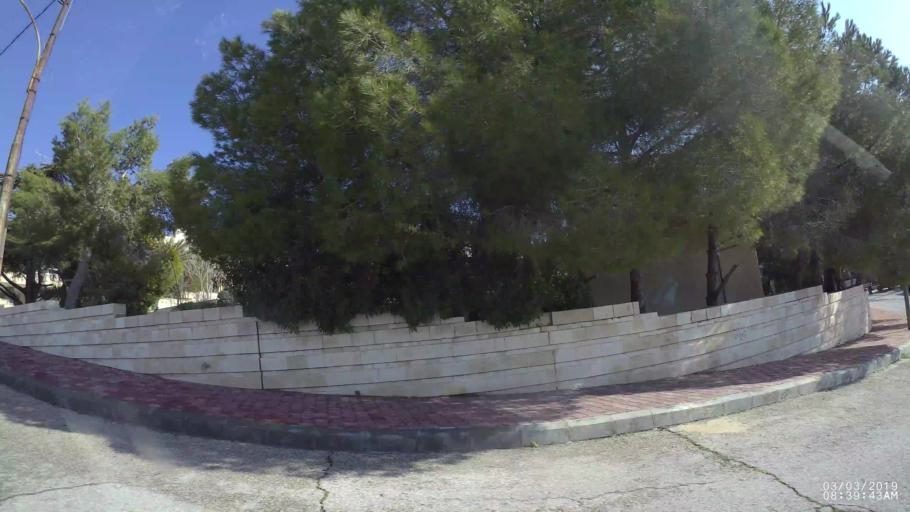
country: JO
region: Amman
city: Al Jubayhah
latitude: 31.9989
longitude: 35.8837
